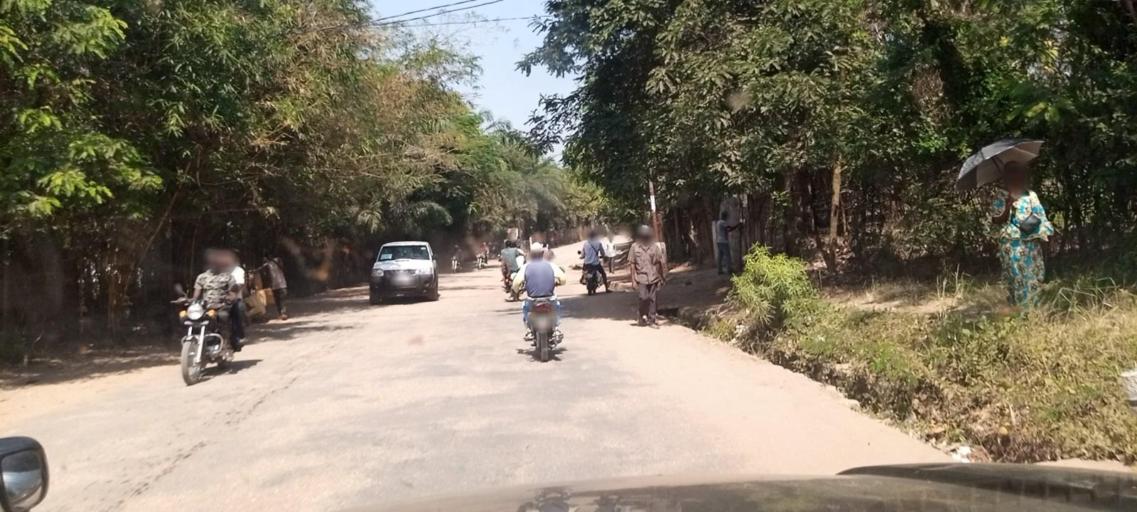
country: CD
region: Kasai-Oriental
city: Mbuji-Mayi
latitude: -6.1221
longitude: 23.5938
